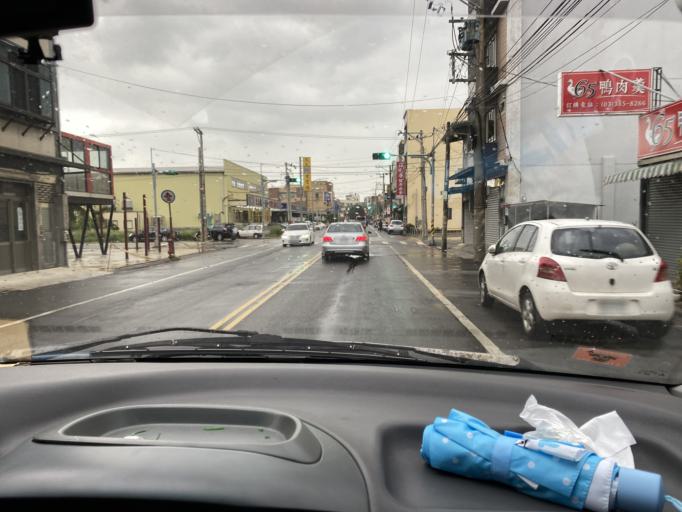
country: TW
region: Taiwan
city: Taoyuan City
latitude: 25.0607
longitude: 121.1995
